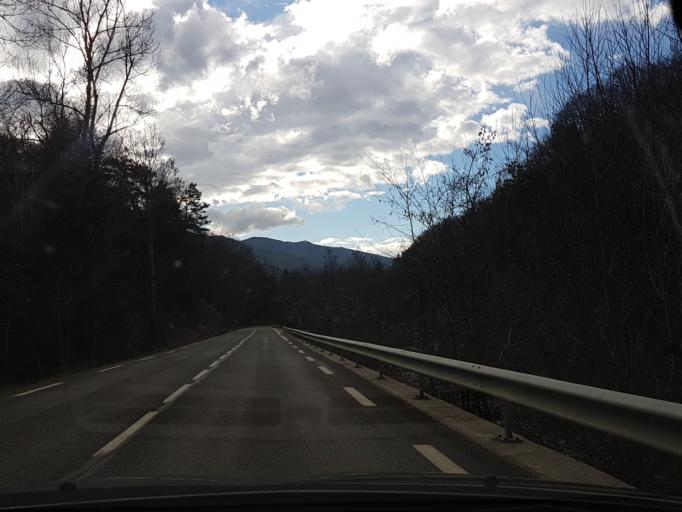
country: FR
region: Provence-Alpes-Cote d'Azur
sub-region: Departement des Hautes-Alpes
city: Tallard
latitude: 44.4883
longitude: 6.0795
